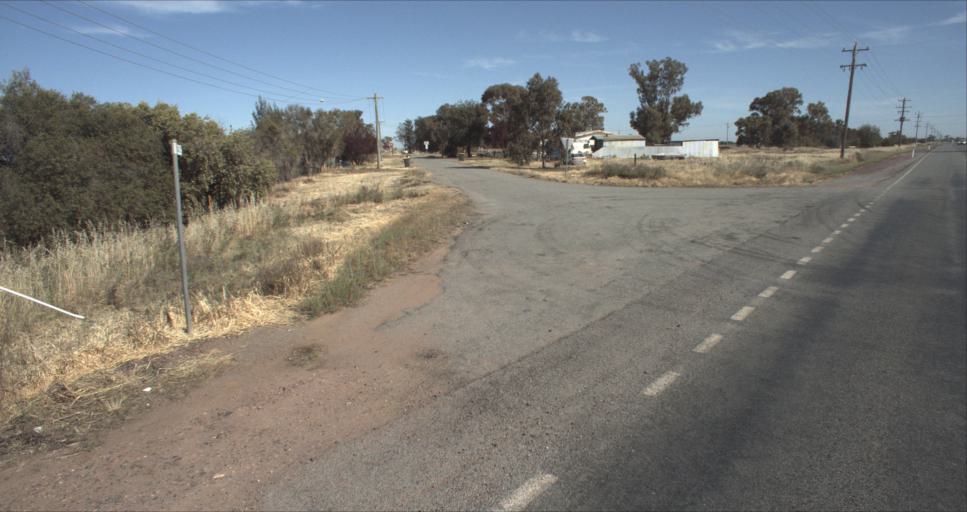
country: AU
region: New South Wales
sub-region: Leeton
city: Leeton
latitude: -34.5977
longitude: 146.4057
